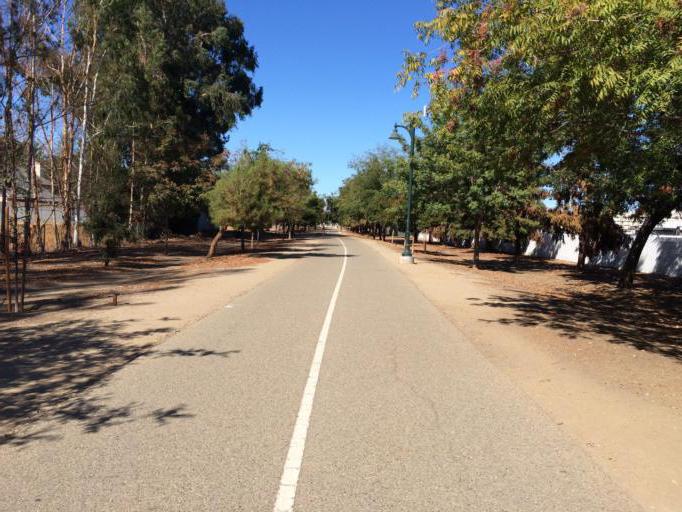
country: US
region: California
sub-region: Fresno County
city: Clovis
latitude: 36.8430
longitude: -119.7150
